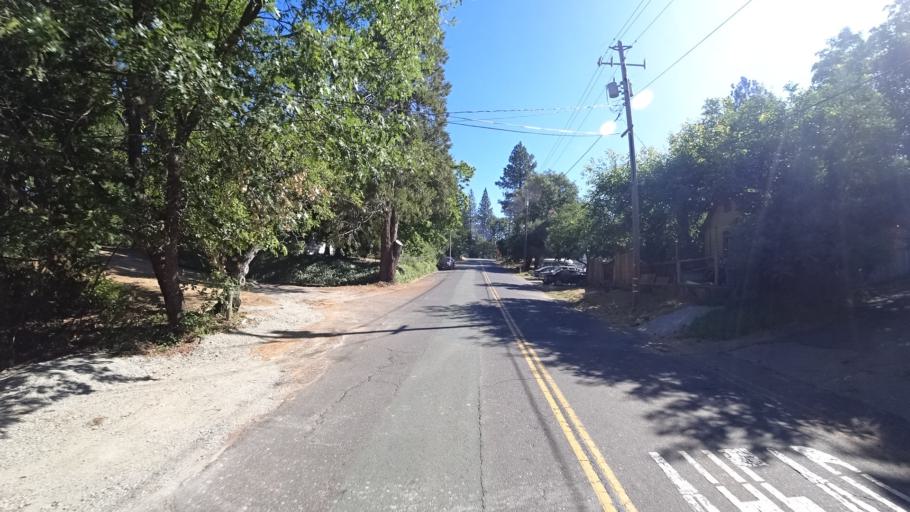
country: US
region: California
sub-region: Amador County
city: Pioneer
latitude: 38.4024
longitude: -120.5279
